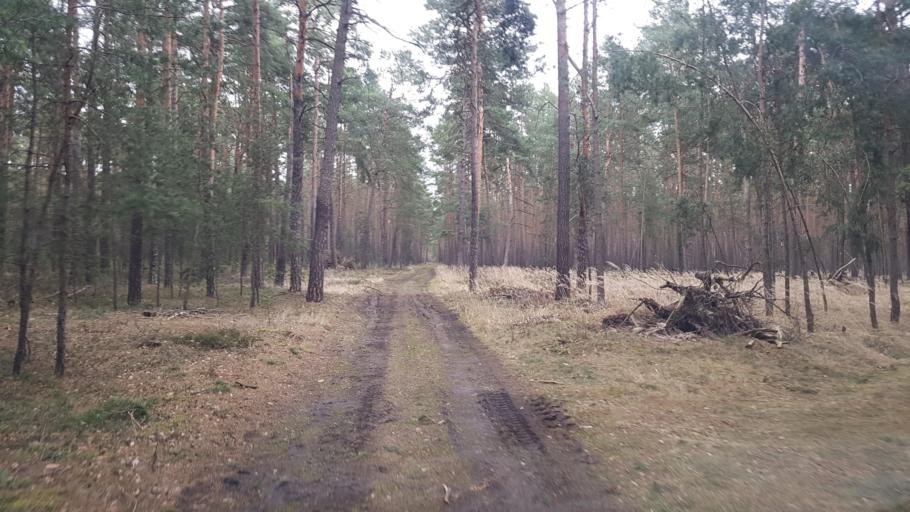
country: DE
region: Brandenburg
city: Ruckersdorf
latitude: 51.5838
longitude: 13.5892
